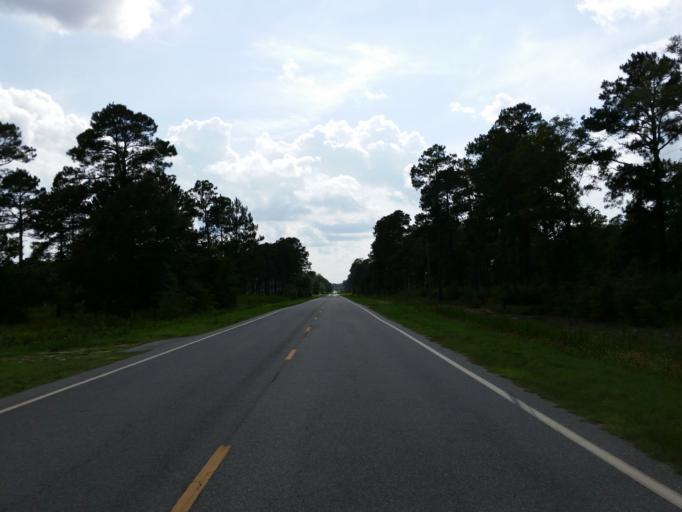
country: US
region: Georgia
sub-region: Lee County
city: Leesburg
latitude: 31.7271
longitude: -83.9796
